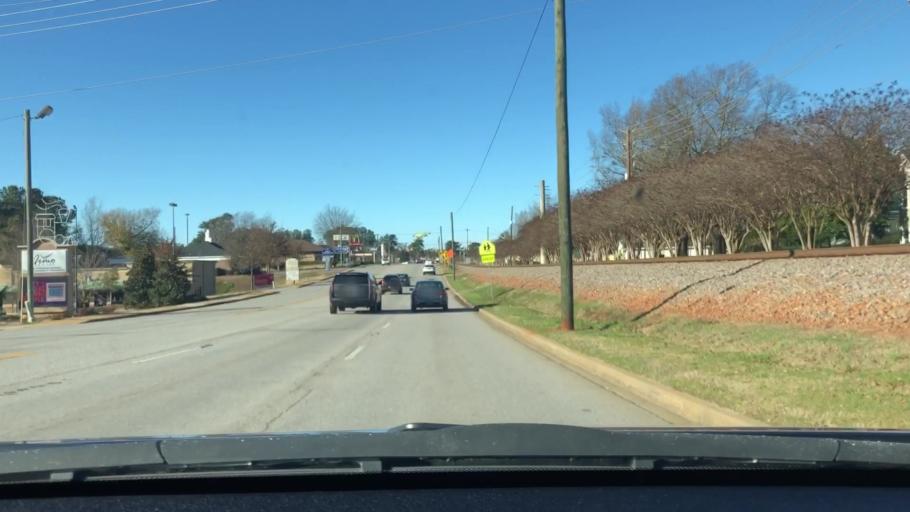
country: US
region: South Carolina
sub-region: Lexington County
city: Irmo
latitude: 34.0830
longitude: -81.1817
